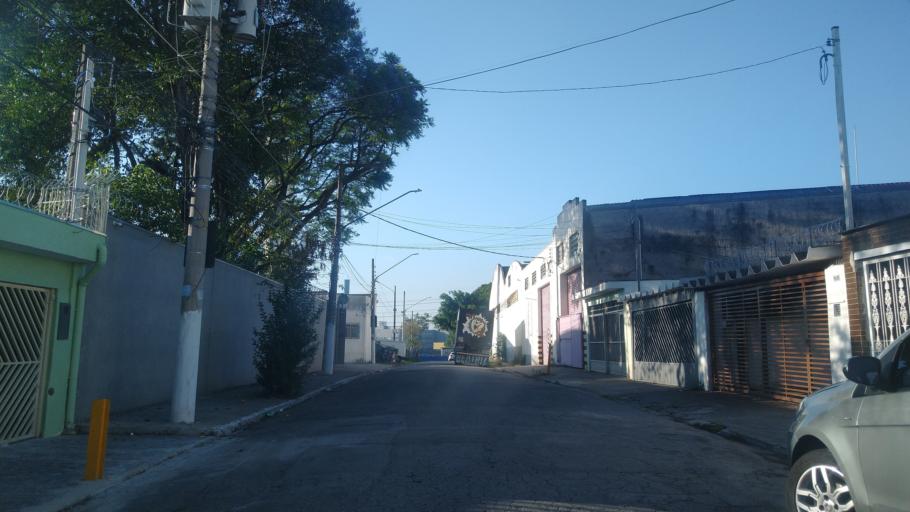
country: BR
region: Sao Paulo
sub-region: Sao Paulo
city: Sao Paulo
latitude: -23.5047
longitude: -46.6106
